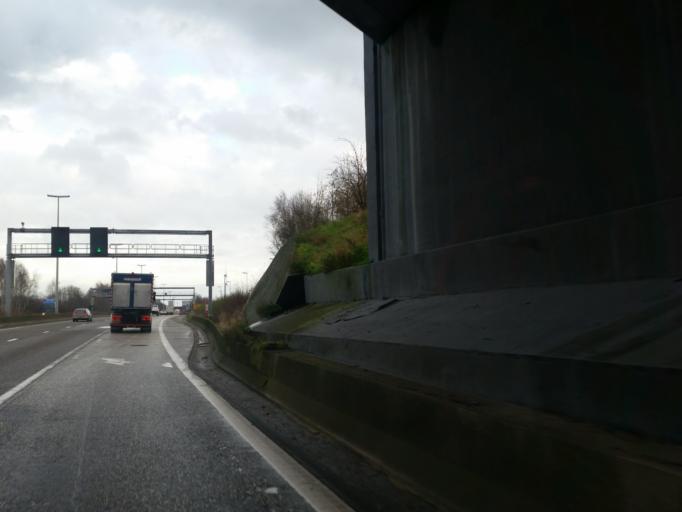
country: BE
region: Flanders
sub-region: Provincie Antwerpen
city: Stabroek
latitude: 51.3034
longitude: 4.3054
